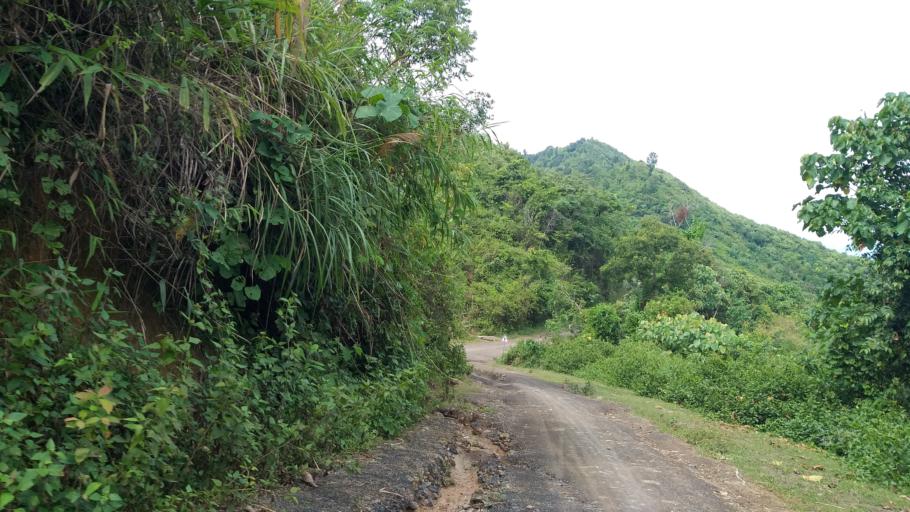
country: VN
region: Huyen Dien Bien
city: Dien Bien Phu
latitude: 21.4676
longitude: 102.6828
